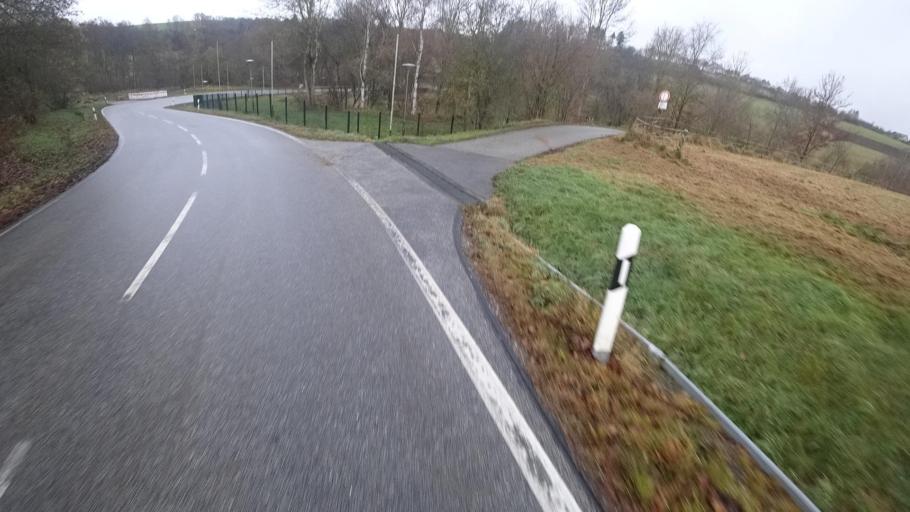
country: DE
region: Rheinland-Pfalz
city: Leiningen
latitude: 50.1382
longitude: 7.5672
